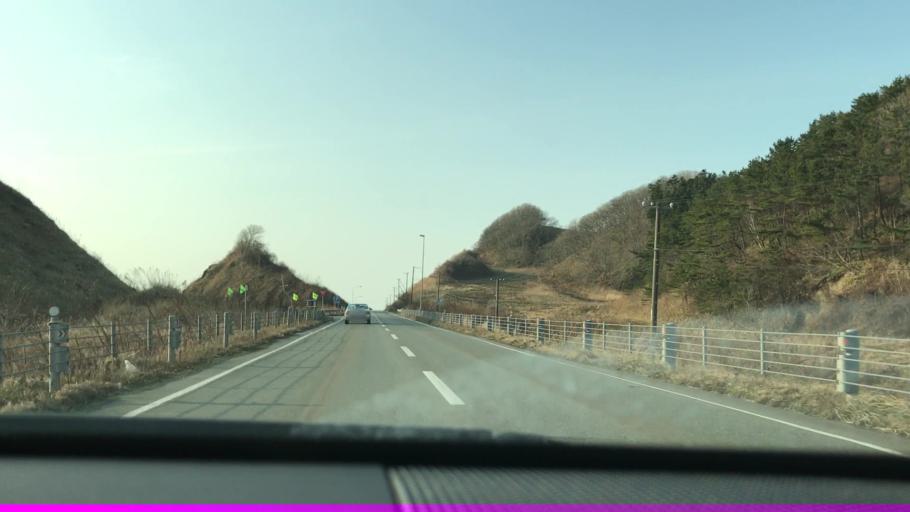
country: JP
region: Hokkaido
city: Shizunai-furukawacho
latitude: 42.2318
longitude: 142.6095
